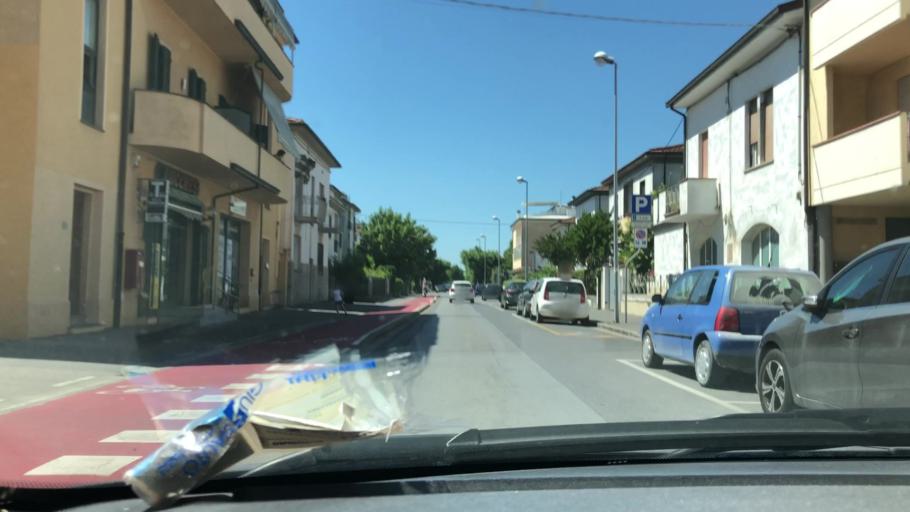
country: IT
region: Tuscany
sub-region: Province of Pisa
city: Pontedera
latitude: 43.6572
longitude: 10.6323
